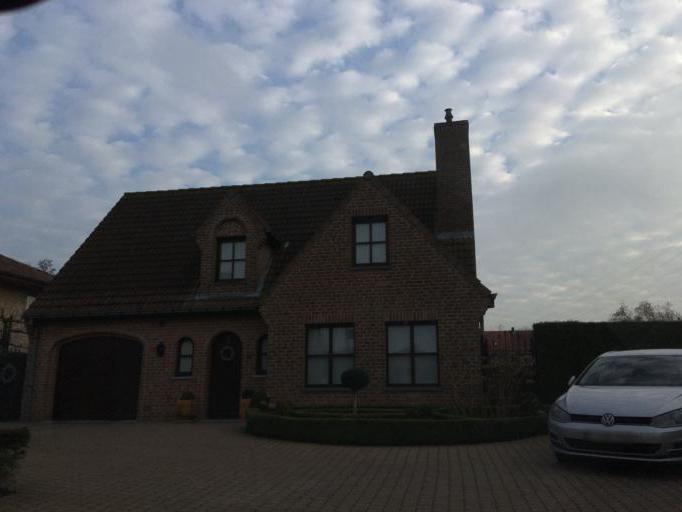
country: BE
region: Flanders
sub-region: Provincie West-Vlaanderen
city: Roeselare
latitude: 50.9338
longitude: 3.1425
